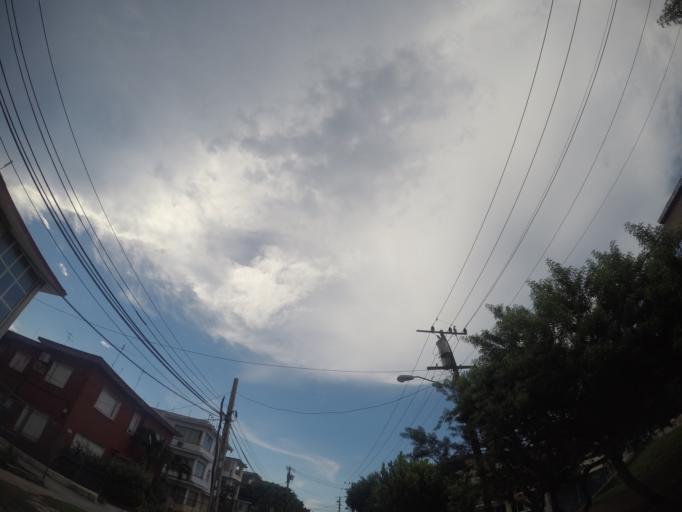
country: CU
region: La Habana
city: Havana
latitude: 23.1222
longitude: -82.4259
